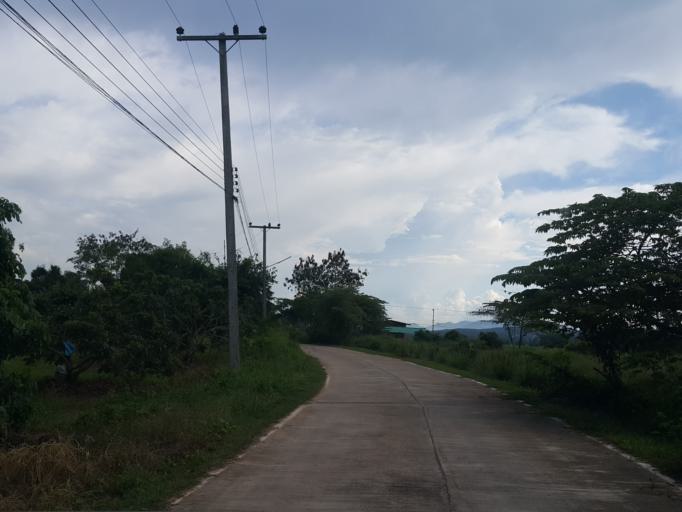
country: TH
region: Chiang Mai
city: Phrao
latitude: 19.3388
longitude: 99.1846
